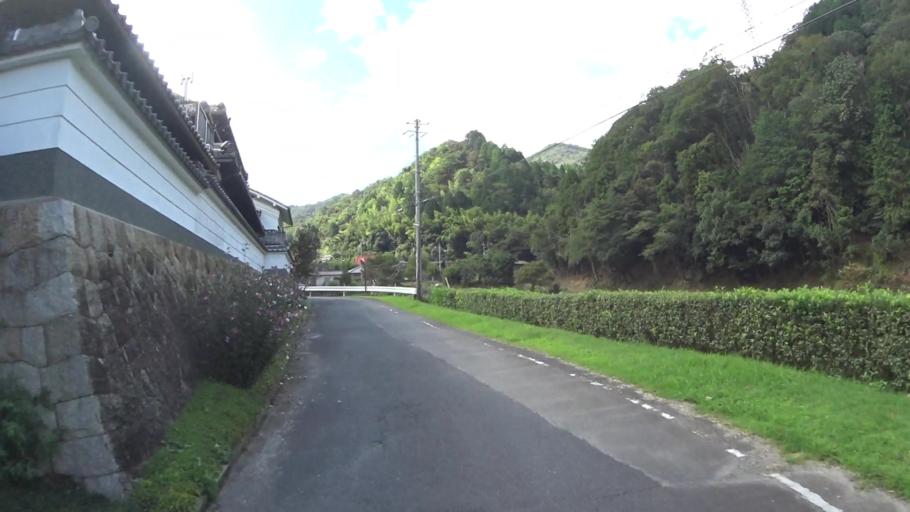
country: JP
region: Shiga Prefecture
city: Otsu-shi
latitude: 34.9491
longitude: 135.8722
